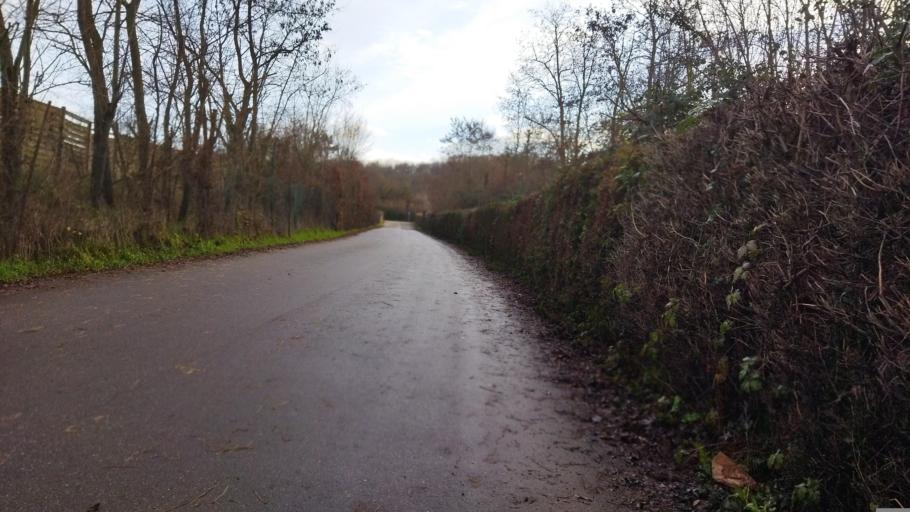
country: DE
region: Baden-Wuerttemberg
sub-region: Regierungsbezirk Stuttgart
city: Oedheim
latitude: 49.2399
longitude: 9.2332
